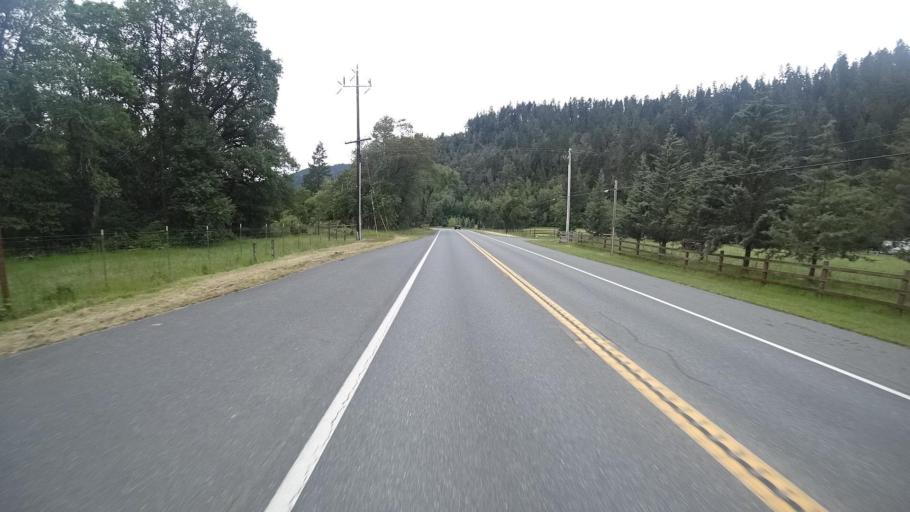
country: US
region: California
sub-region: Humboldt County
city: Willow Creek
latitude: 40.9568
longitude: -123.6432
